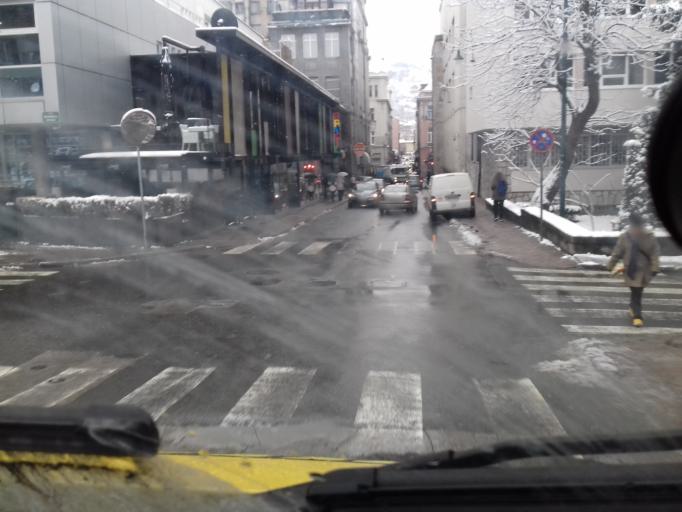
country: BA
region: Federation of Bosnia and Herzegovina
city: Kobilja Glava
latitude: 43.8598
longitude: 18.4204
